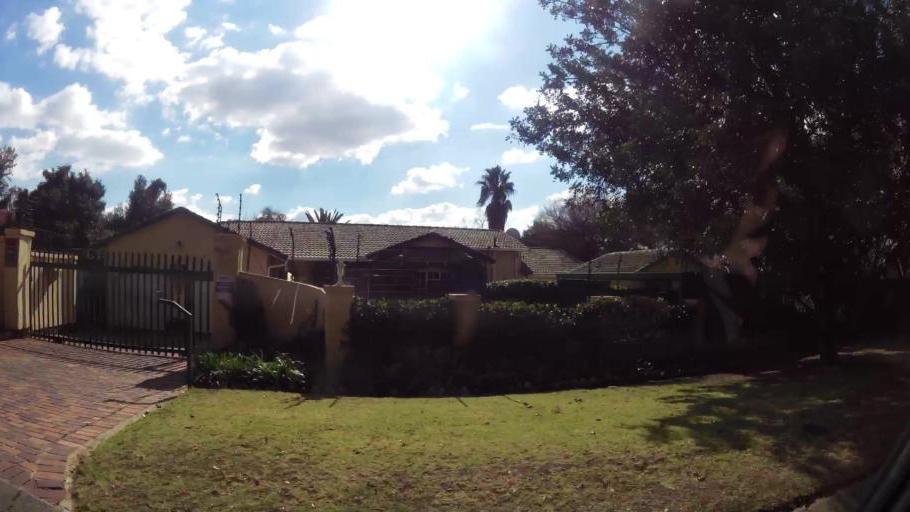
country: ZA
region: Gauteng
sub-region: City of Johannesburg Metropolitan Municipality
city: Roodepoort
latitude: -26.0739
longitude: 27.9686
